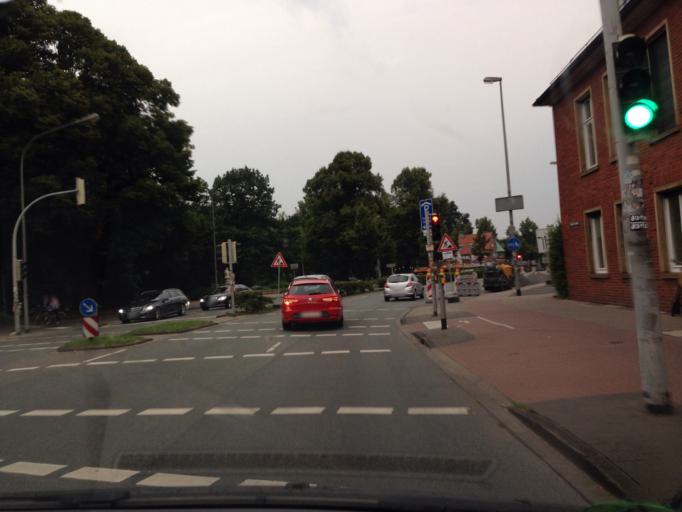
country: DE
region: North Rhine-Westphalia
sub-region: Regierungsbezirk Munster
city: Muenster
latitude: 51.9560
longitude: 7.6196
